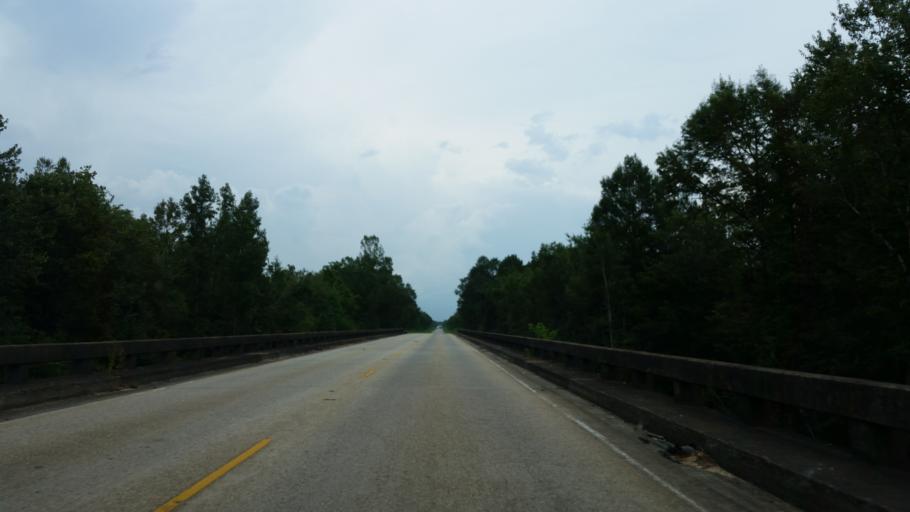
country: US
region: Florida
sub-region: Escambia County
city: Molino
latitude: 30.6659
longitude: -87.2839
